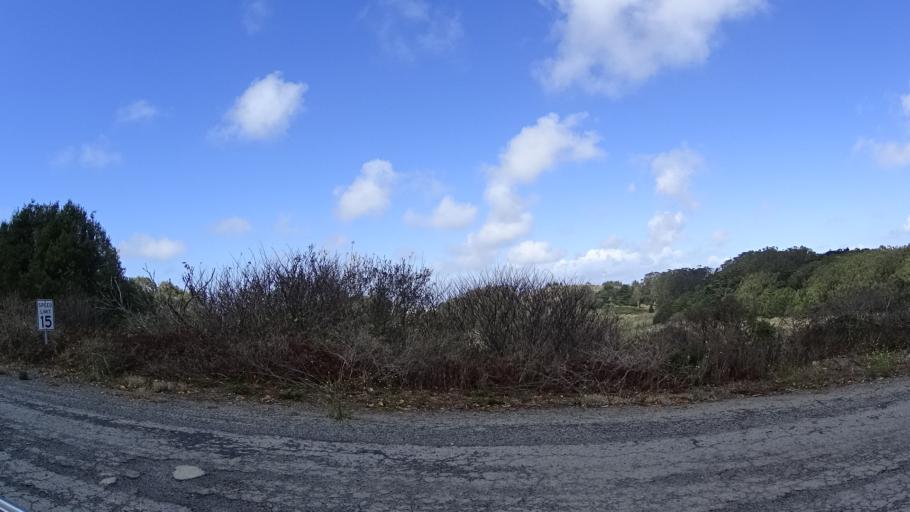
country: US
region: California
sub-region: San Mateo County
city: Daly City
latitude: 37.6949
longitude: -122.4363
